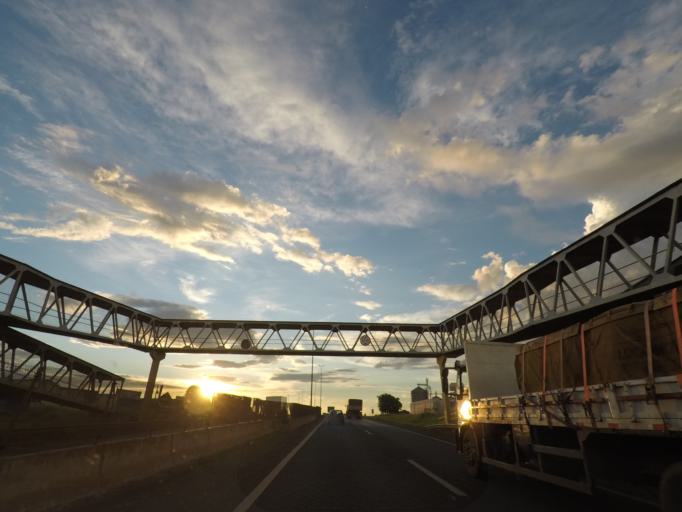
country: BR
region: Minas Gerais
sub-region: Uberaba
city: Uberaba
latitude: -19.7790
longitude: -47.9403
